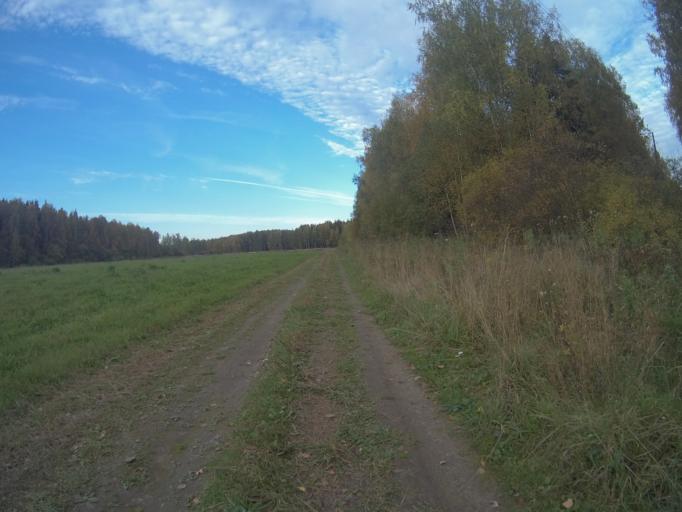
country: RU
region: Vladimir
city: Golovino
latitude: 55.9709
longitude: 40.3980
